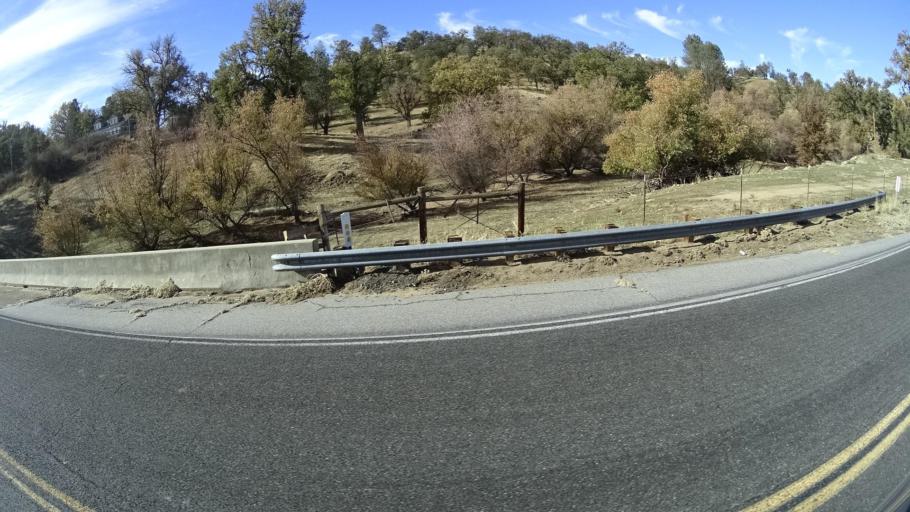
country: US
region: California
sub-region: Kern County
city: Alta Sierra
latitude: 35.7071
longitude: -118.7259
